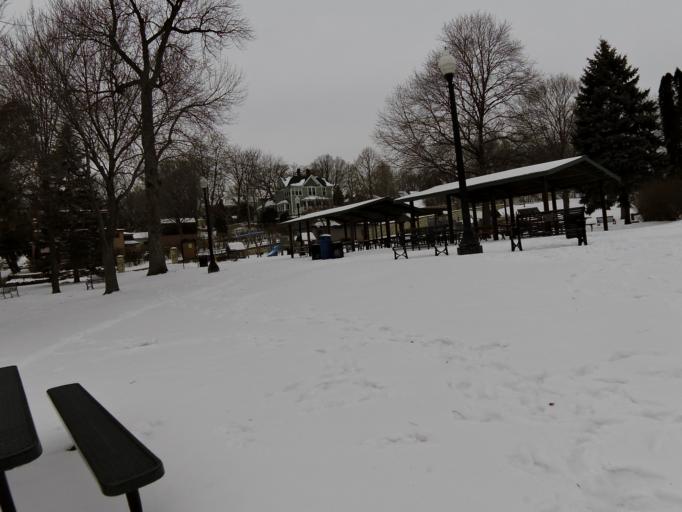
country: US
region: Minnesota
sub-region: Washington County
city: Stillwater
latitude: 45.0604
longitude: -92.8084
